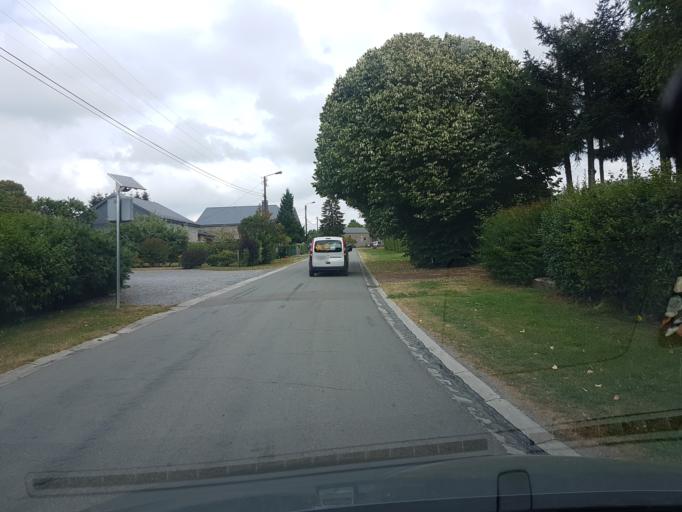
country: BE
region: Wallonia
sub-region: Province du Luxembourg
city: Manhay
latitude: 50.2744
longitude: 5.6572
